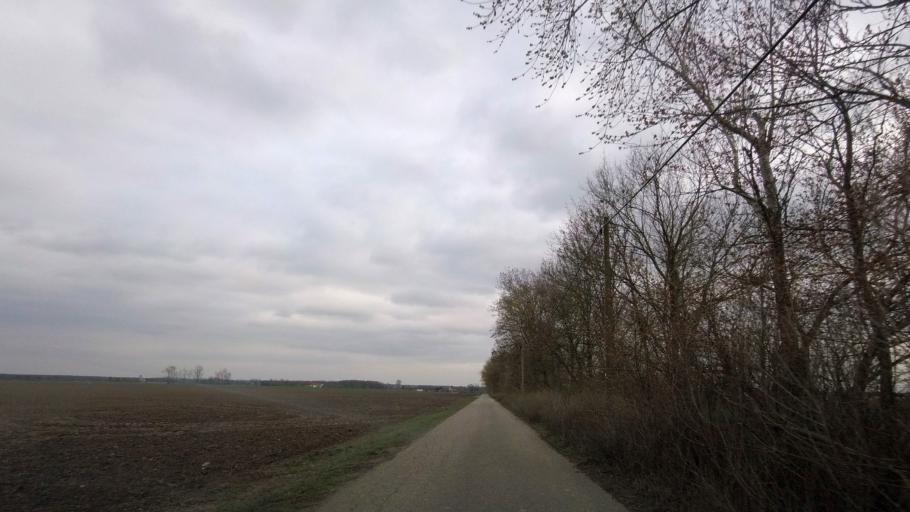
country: DE
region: Saxony-Anhalt
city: Seyda
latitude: 51.9011
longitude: 12.8897
